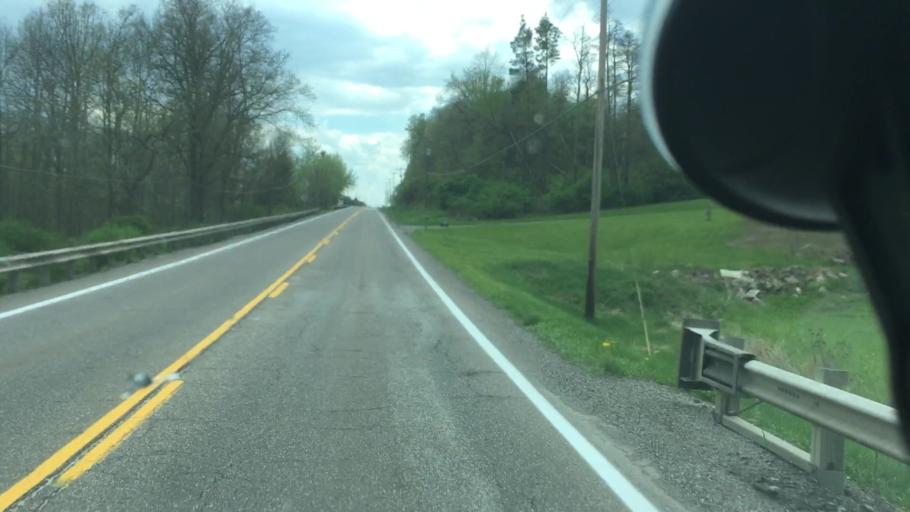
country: US
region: Ohio
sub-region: Columbiana County
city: Columbiana
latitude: 40.9122
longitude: -80.6936
